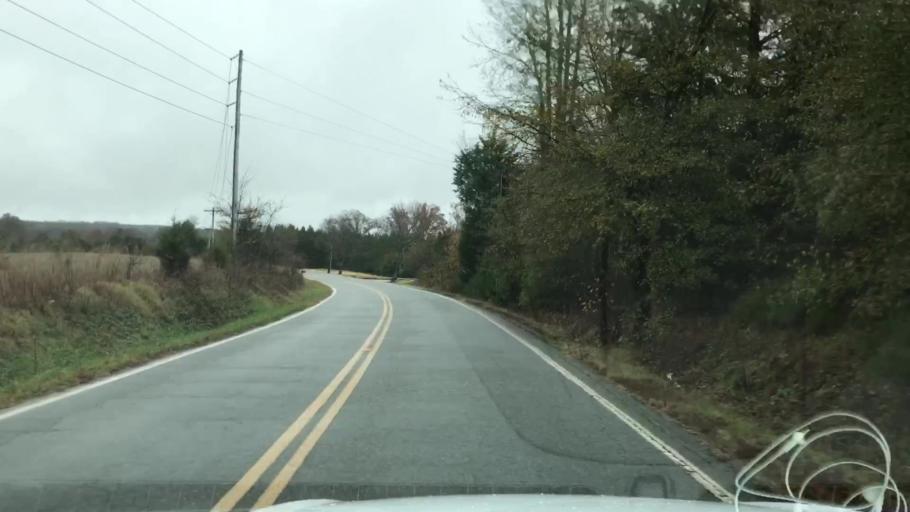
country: US
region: South Carolina
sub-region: Spartanburg County
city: Woodruff
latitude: 34.7486
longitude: -81.9354
